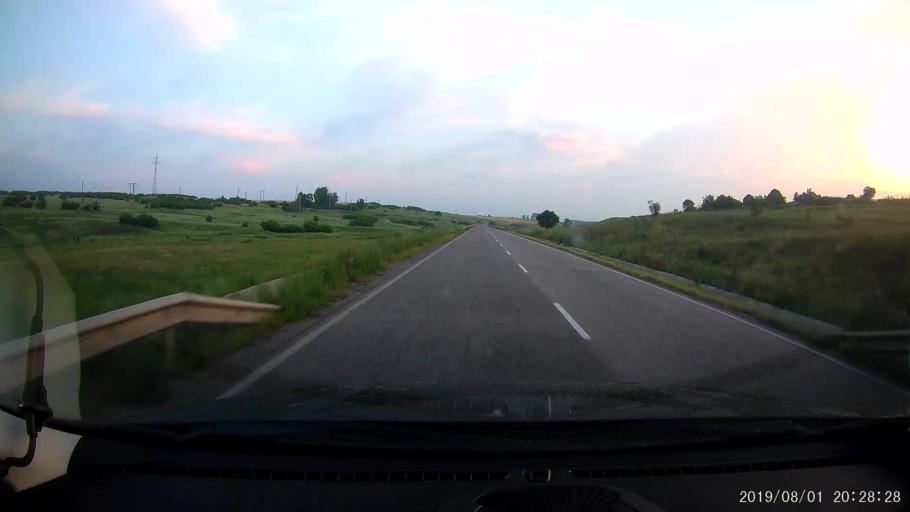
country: BG
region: Yambol
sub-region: Obshtina Elkhovo
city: Elkhovo
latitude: 42.1684
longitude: 26.5773
